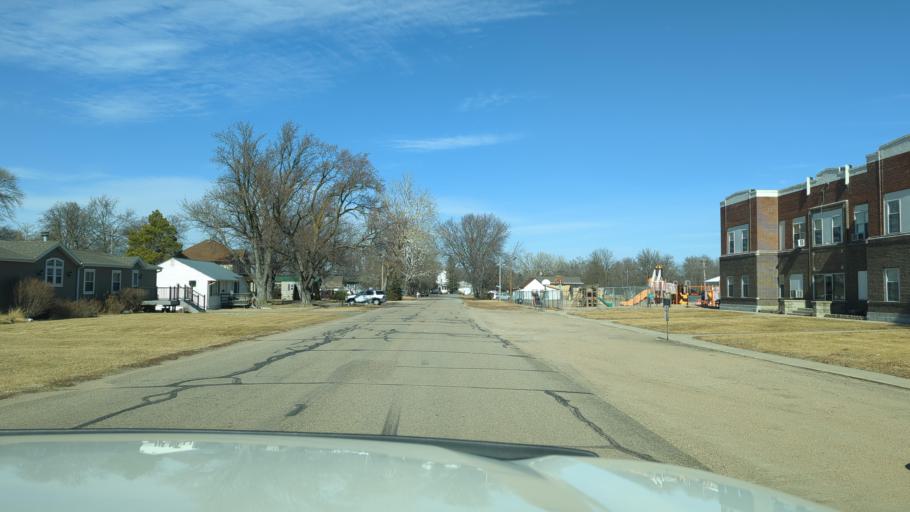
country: US
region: Nebraska
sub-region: Antelope County
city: Neligh
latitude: 42.2604
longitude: -98.3451
